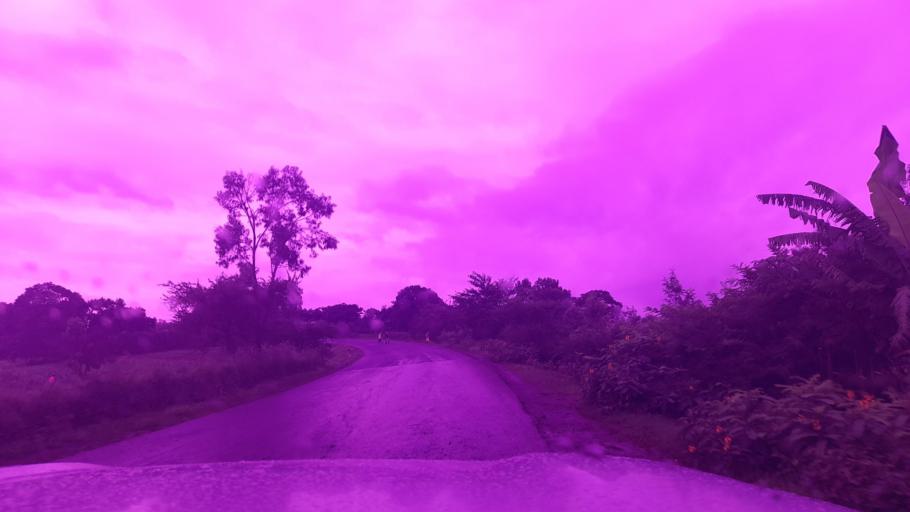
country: ET
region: Oromiya
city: Jima
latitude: 7.7138
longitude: 37.2526
